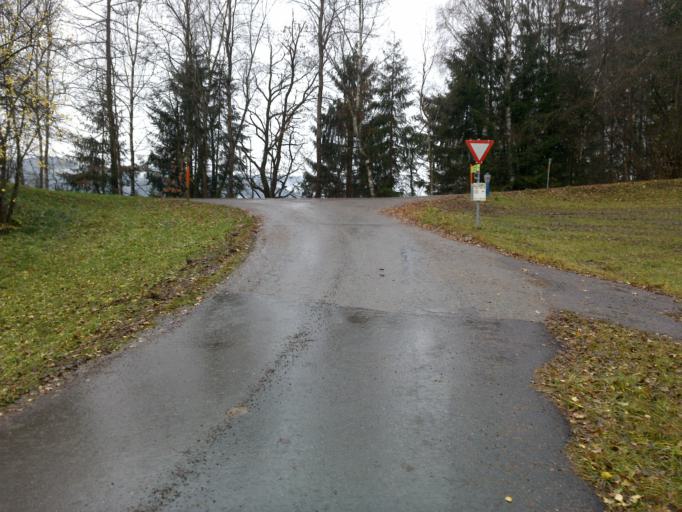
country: AT
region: Styria
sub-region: Politischer Bezirk Murtal
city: Seckau
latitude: 47.2823
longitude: 14.7959
